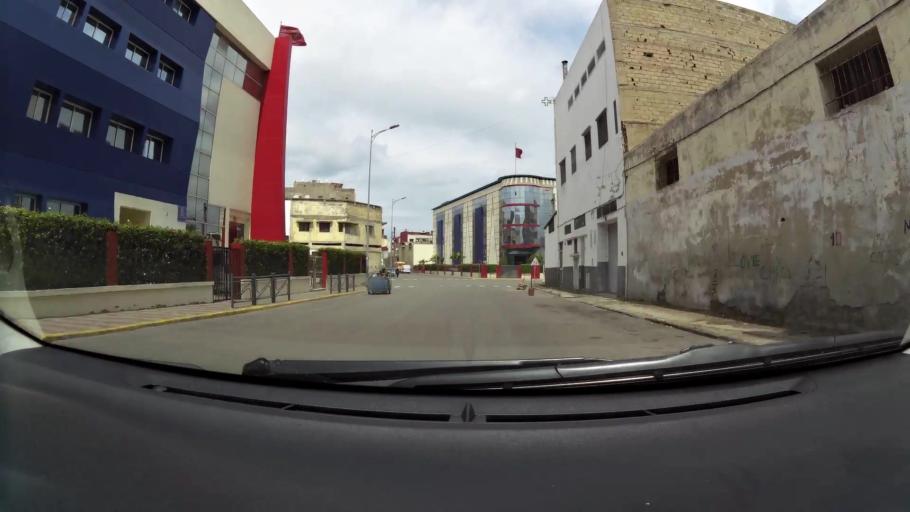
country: MA
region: Grand Casablanca
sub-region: Casablanca
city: Casablanca
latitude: 33.5873
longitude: -7.5738
